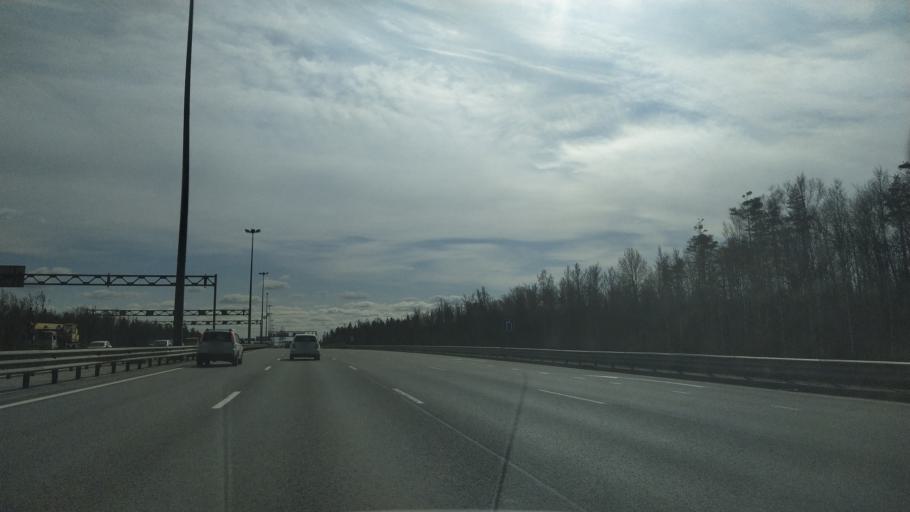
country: RU
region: St.-Petersburg
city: Krasnogvargeisky
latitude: 59.9427
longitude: 30.5394
